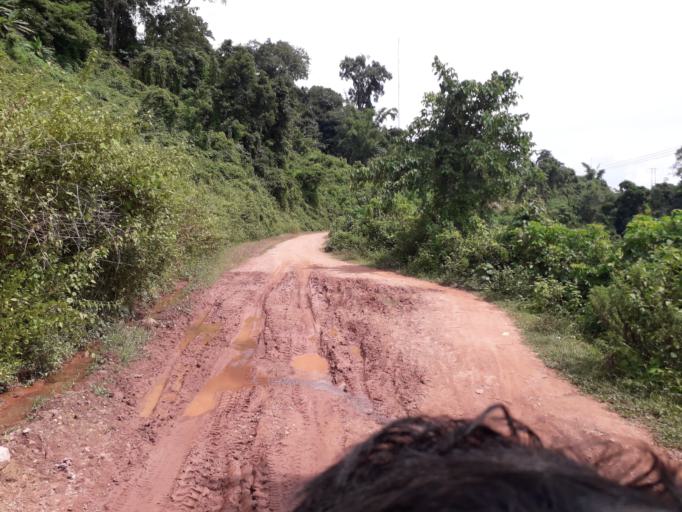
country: CN
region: Yunnan
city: Menglie
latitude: 22.1953
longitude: 101.7319
